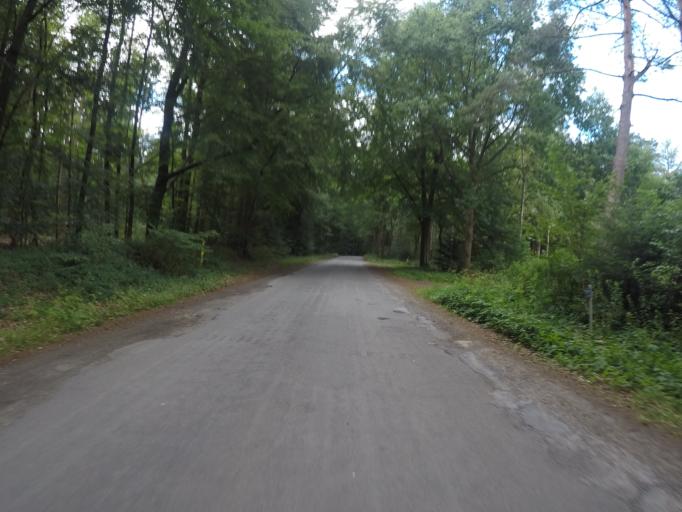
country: DE
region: Lower Saxony
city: Cadenberge
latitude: 53.7525
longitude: 9.0517
